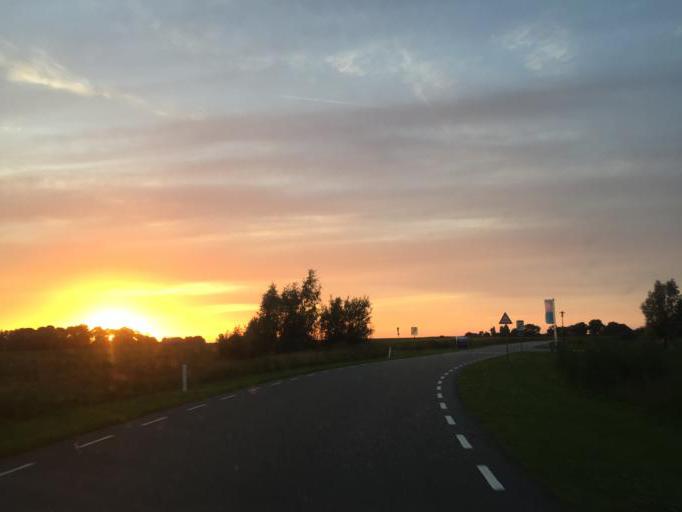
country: NL
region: Friesland
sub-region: Gemeente Dongeradeel
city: Anjum
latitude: 53.3757
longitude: 6.1534
